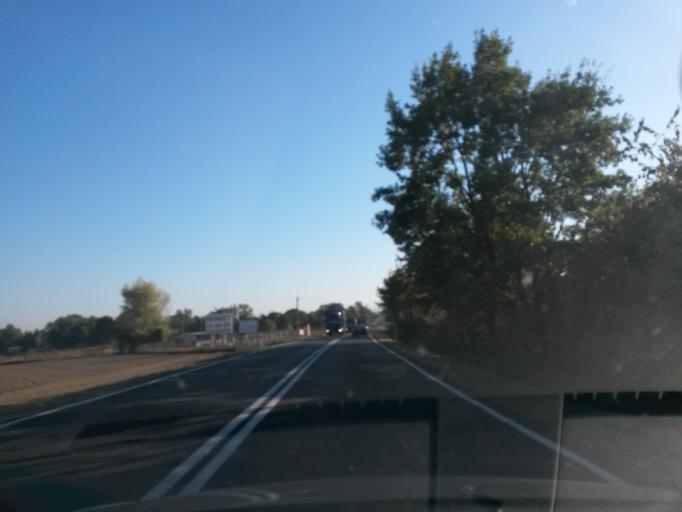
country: PL
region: Lower Silesian Voivodeship
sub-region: Powiat swidnicki
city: Strzegom
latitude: 50.9663
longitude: 16.3664
